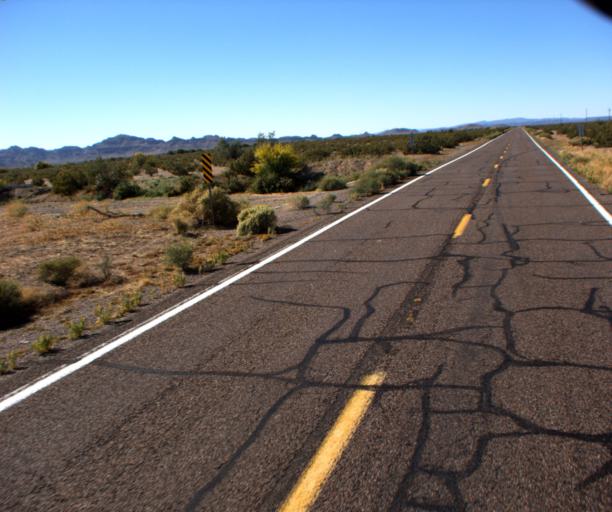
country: US
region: Arizona
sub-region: Maricopa County
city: Gila Bend
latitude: 32.7463
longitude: -112.8283
